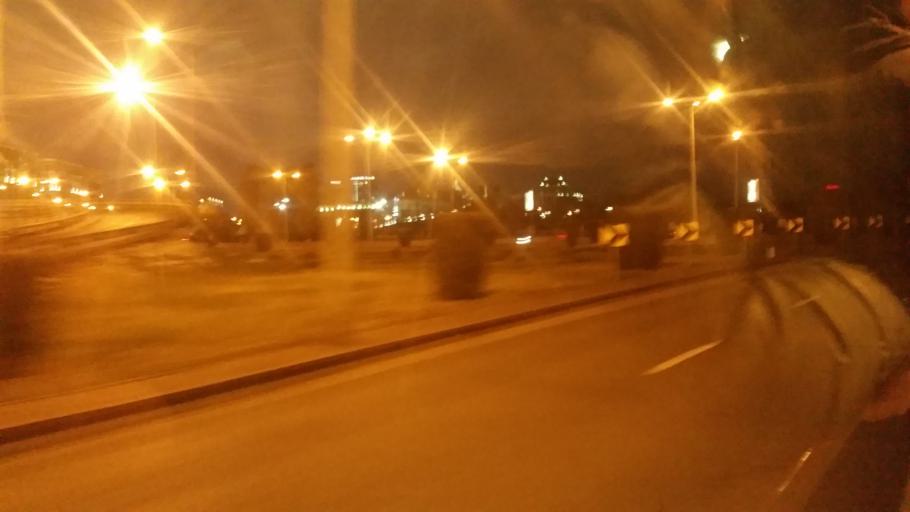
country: KZ
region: Astana Qalasy
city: Astana
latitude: 51.1329
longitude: 71.4416
